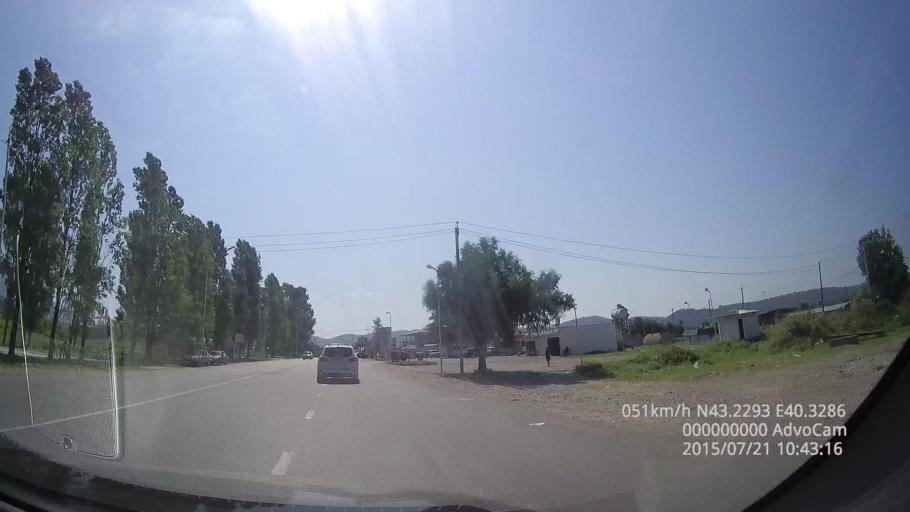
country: GE
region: Abkhazia
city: Bich'vinta
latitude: 43.2293
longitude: 40.3288
